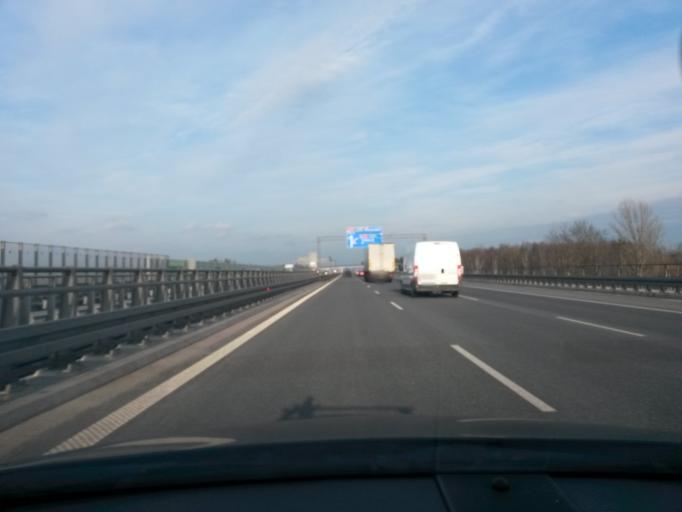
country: PL
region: Lodz Voivodeship
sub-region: Powiat zgierski
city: Strykow
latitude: 51.8895
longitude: 19.6050
